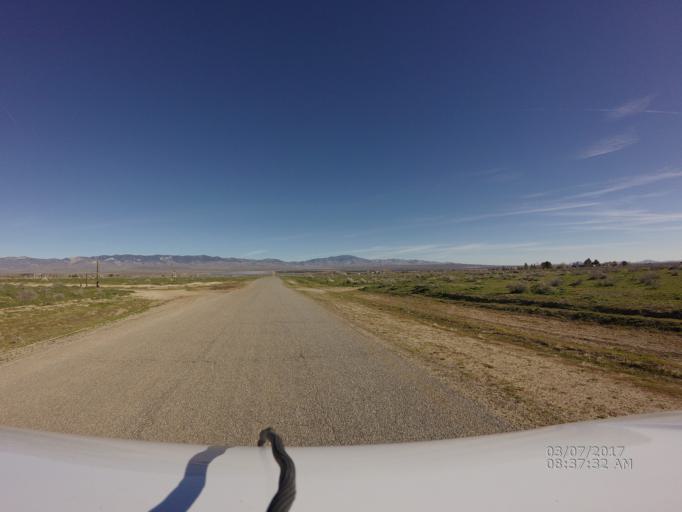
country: US
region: California
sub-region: Los Angeles County
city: Green Valley
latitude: 34.7926
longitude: -118.5457
